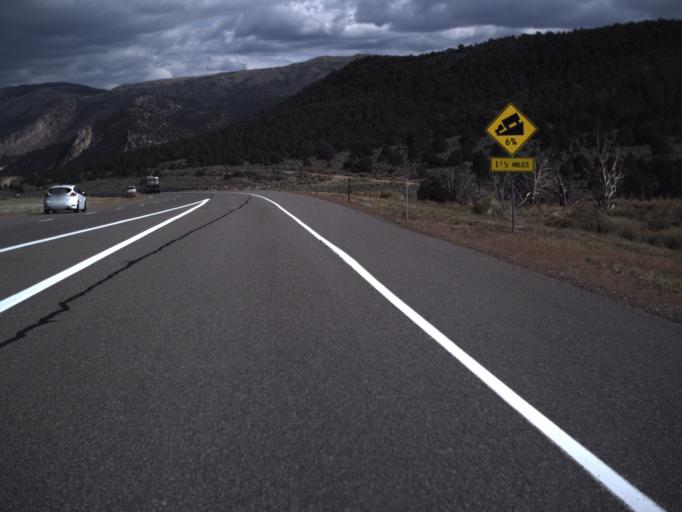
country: US
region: Utah
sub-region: Sevier County
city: Monroe
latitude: 38.5513
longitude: -112.4045
